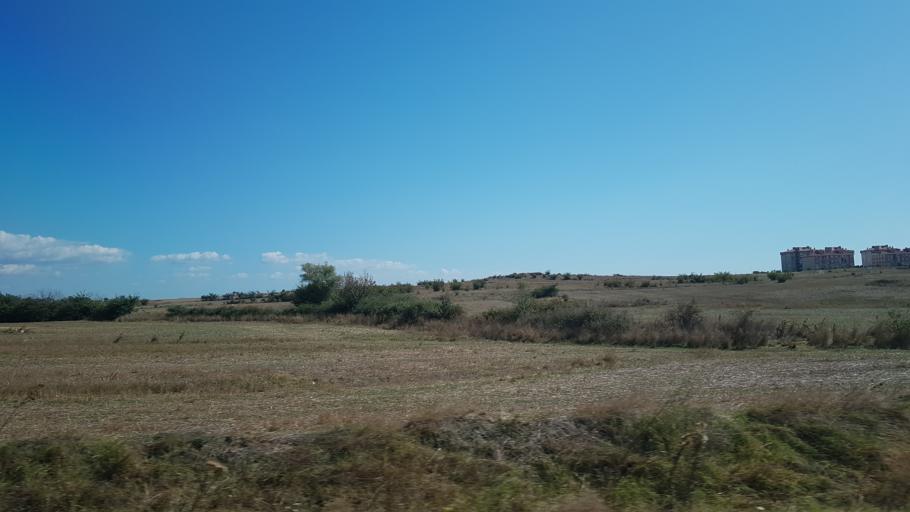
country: TR
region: Kirklareli
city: Kirklareli
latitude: 41.7623
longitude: 27.2216
